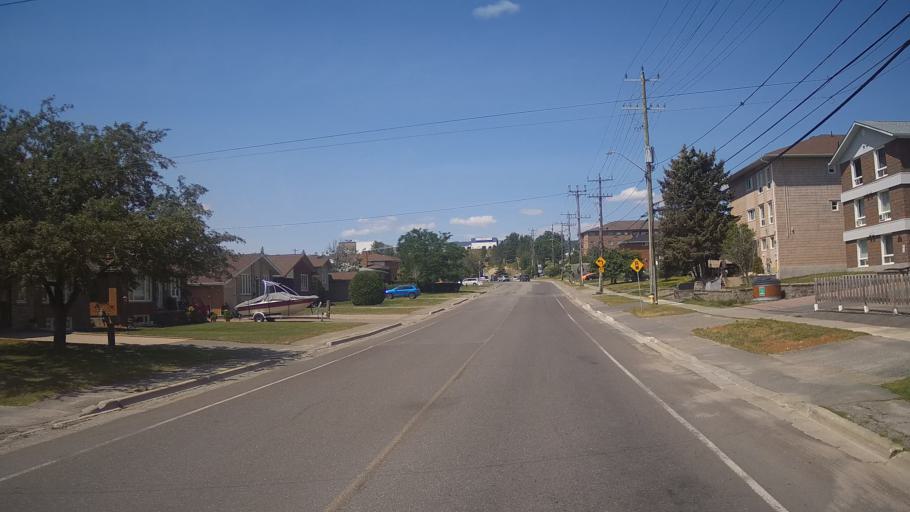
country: CA
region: Ontario
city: Greater Sudbury
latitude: 46.4624
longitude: -81.0281
